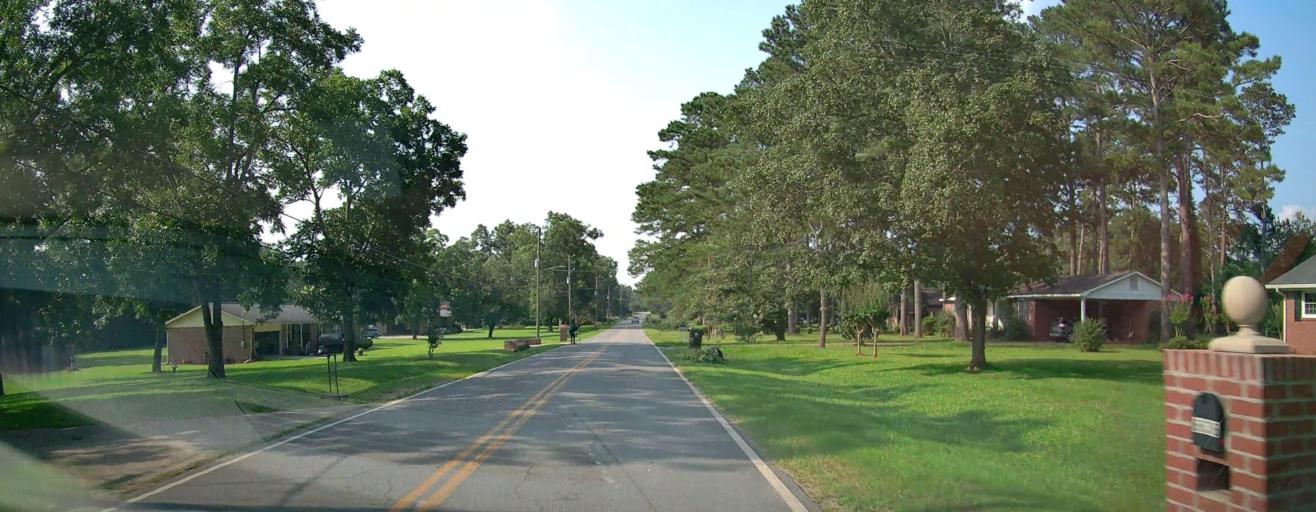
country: US
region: Georgia
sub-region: Houston County
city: Centerville
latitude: 32.7274
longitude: -83.6891
